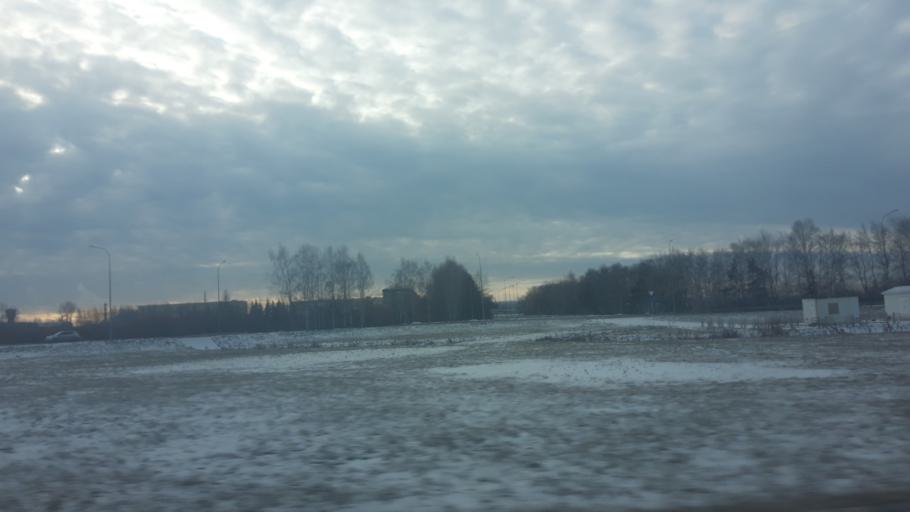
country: RU
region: Tjumen
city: Moskovskiy
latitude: 57.1867
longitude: 65.3592
